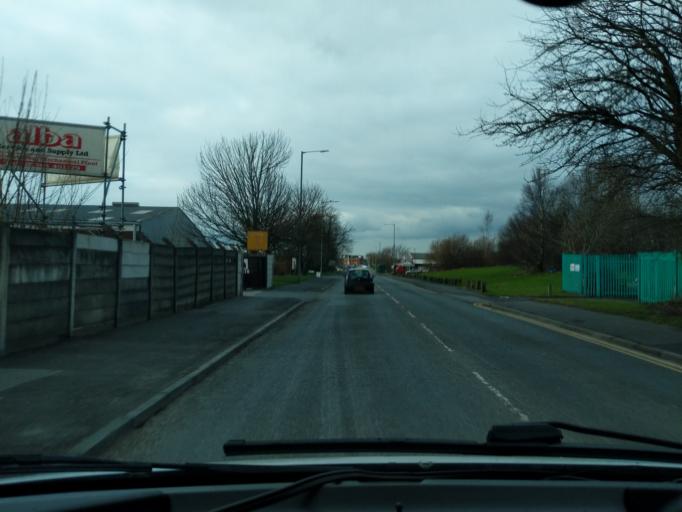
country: GB
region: England
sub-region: St. Helens
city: St Helens
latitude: 53.4471
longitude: -2.7201
